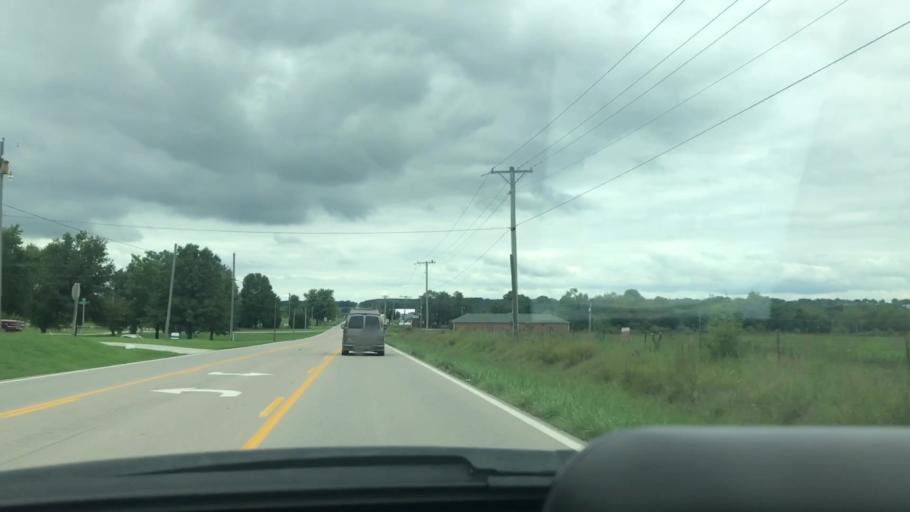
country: US
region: Missouri
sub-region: Dallas County
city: Buffalo
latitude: 37.6523
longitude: -93.1038
